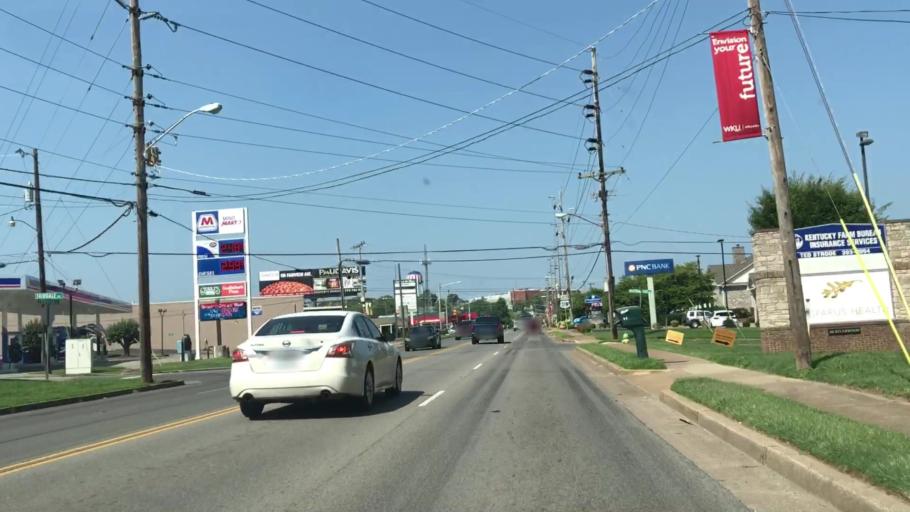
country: US
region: Kentucky
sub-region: Warren County
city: Bowling Green
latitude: 36.9907
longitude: -86.4252
